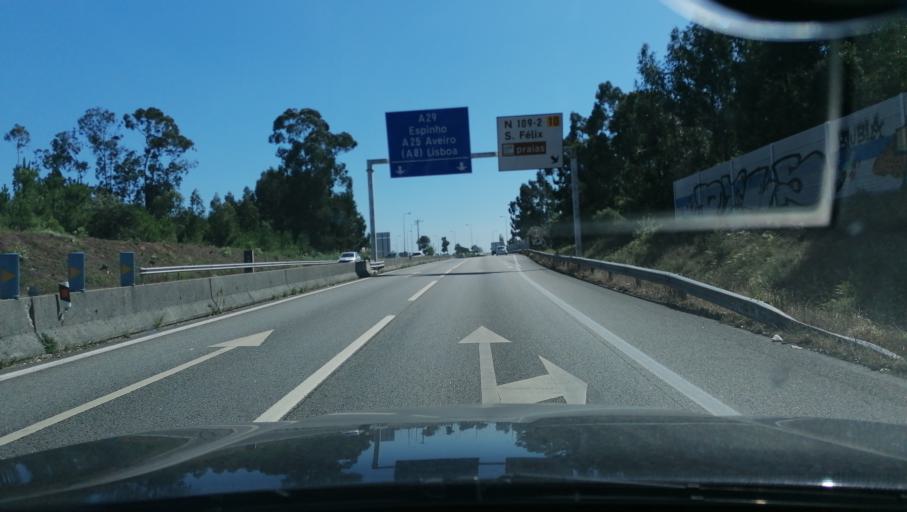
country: PT
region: Porto
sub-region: Vila Nova de Gaia
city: Sao Felix da Marinha
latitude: 41.0283
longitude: -8.6244
